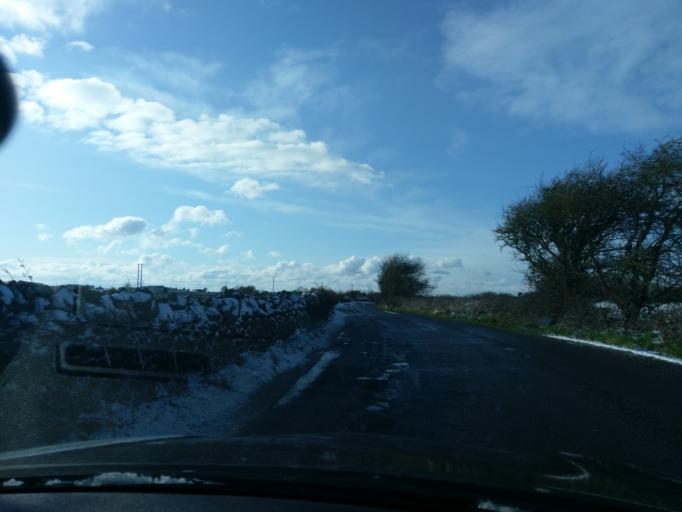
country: IE
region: Connaught
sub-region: County Galway
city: Oranmore
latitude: 53.1986
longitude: -8.8416
